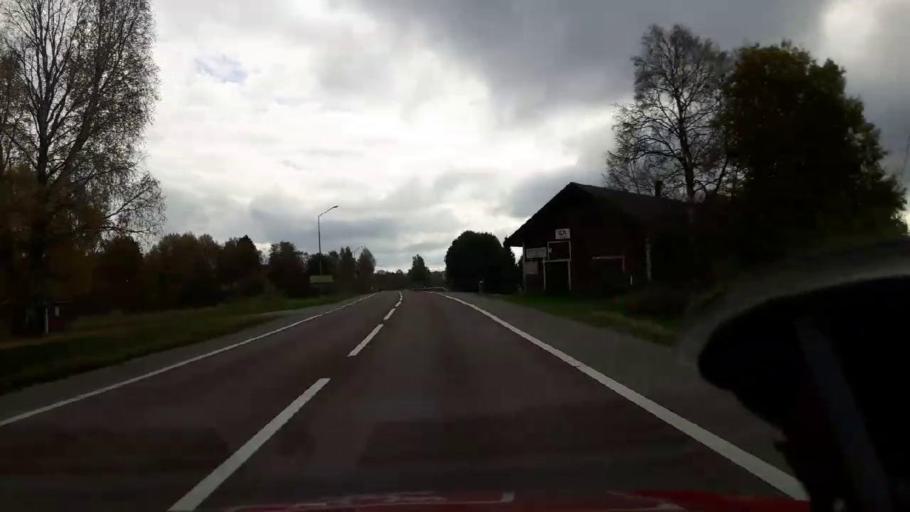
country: SE
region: Jaemtland
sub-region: Harjedalens Kommun
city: Sveg
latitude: 62.1752
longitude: 14.9184
